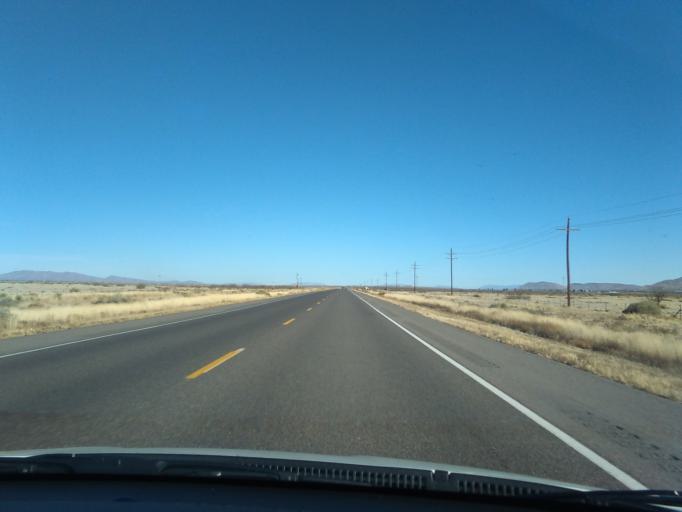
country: US
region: New Mexico
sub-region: Dona Ana County
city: Hatch
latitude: 32.5969
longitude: -107.3381
